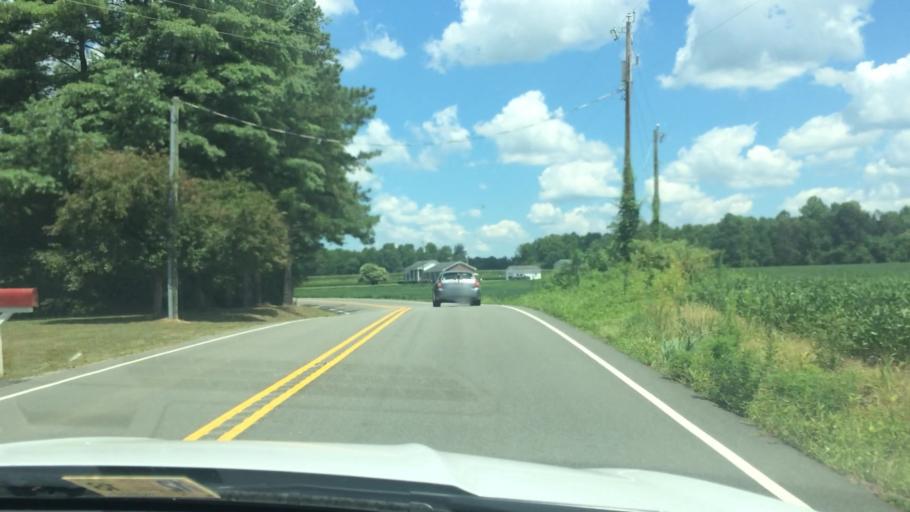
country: US
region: Virginia
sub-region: King William County
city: West Point
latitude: 37.5966
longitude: -76.7646
